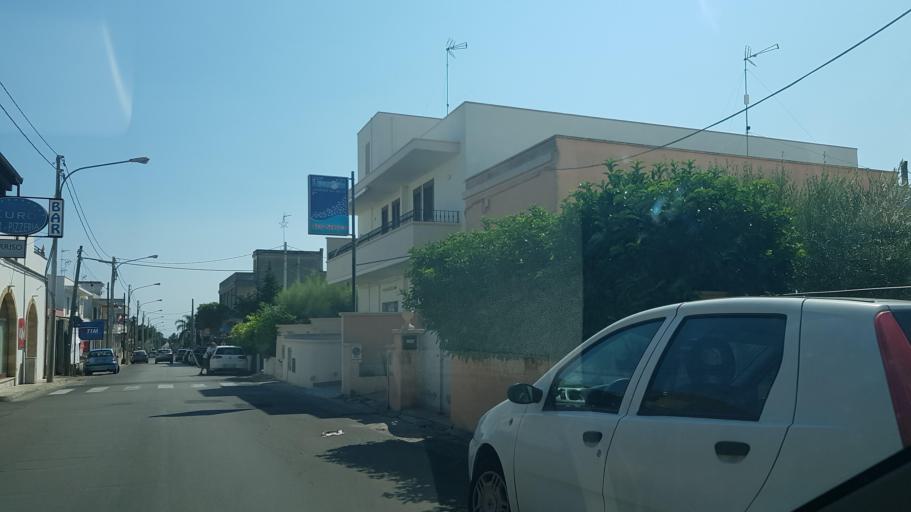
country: IT
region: Apulia
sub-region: Provincia di Lecce
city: Ugento
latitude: 39.9226
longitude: 18.1574
